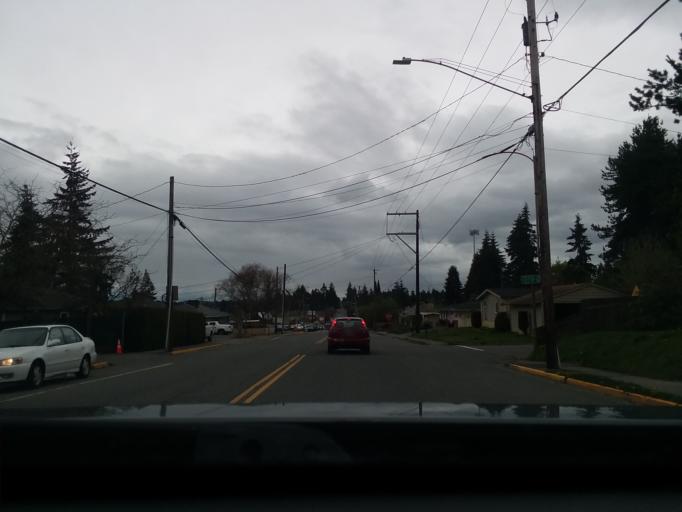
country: US
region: Washington
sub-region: Snohomish County
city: Esperance
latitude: 47.7969
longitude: -122.3356
